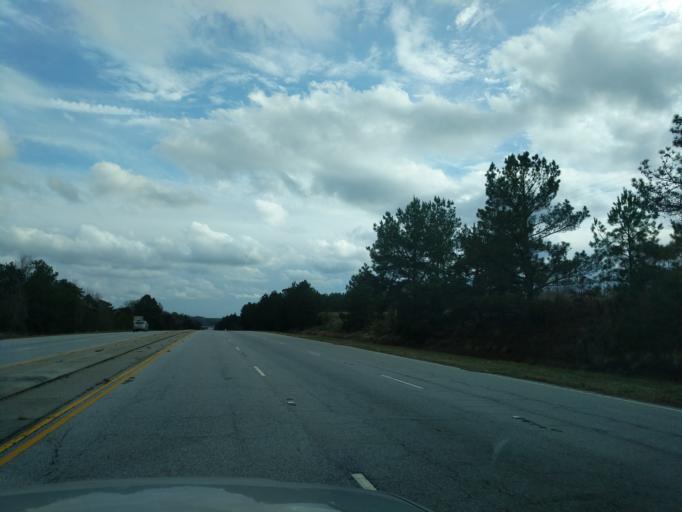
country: US
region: South Carolina
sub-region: Greenwood County
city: Ware Shoals
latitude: 34.4243
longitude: -82.2361
